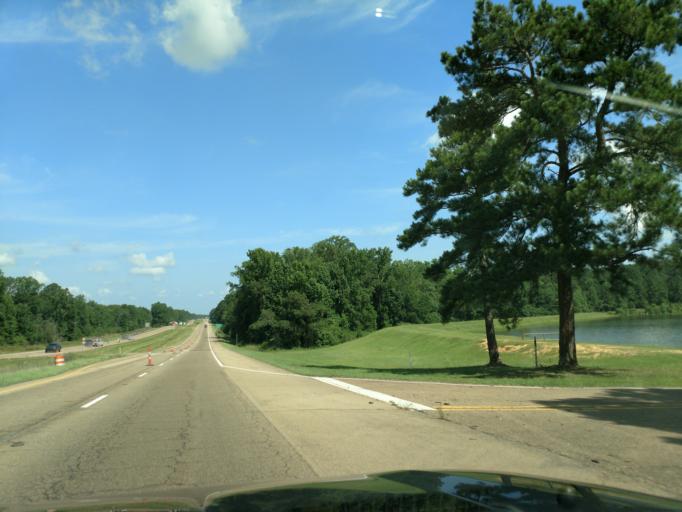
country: US
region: Mississippi
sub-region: Simpson County
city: Magee
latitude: 31.9116
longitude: -89.7936
